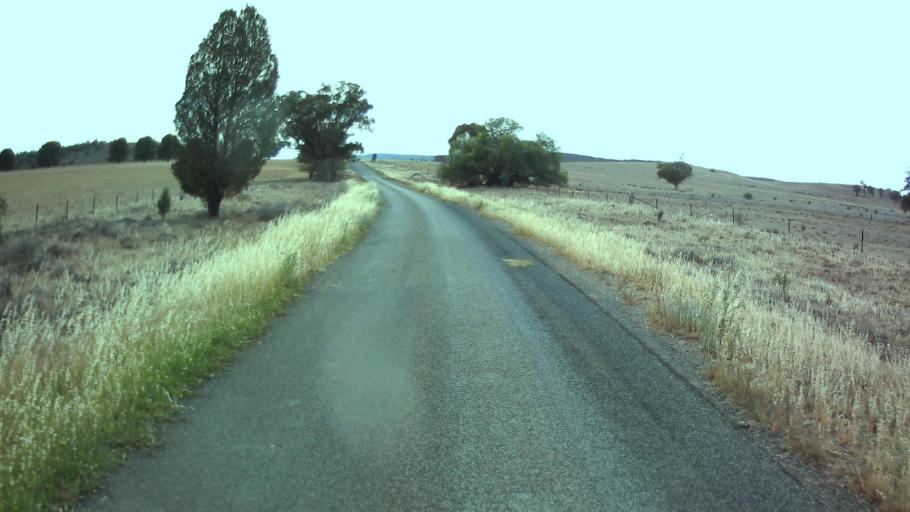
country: AU
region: New South Wales
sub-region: Weddin
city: Grenfell
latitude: -33.8456
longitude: 148.2487
